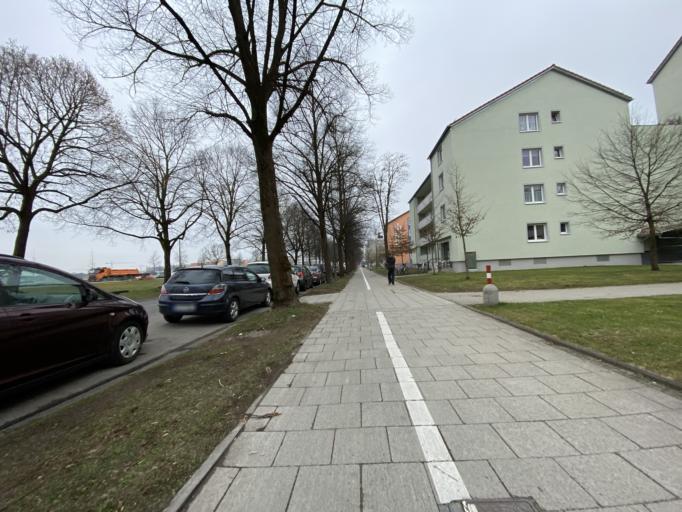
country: DE
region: Bavaria
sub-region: Upper Bavaria
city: Oberschleissheim
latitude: 48.2175
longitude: 11.5614
